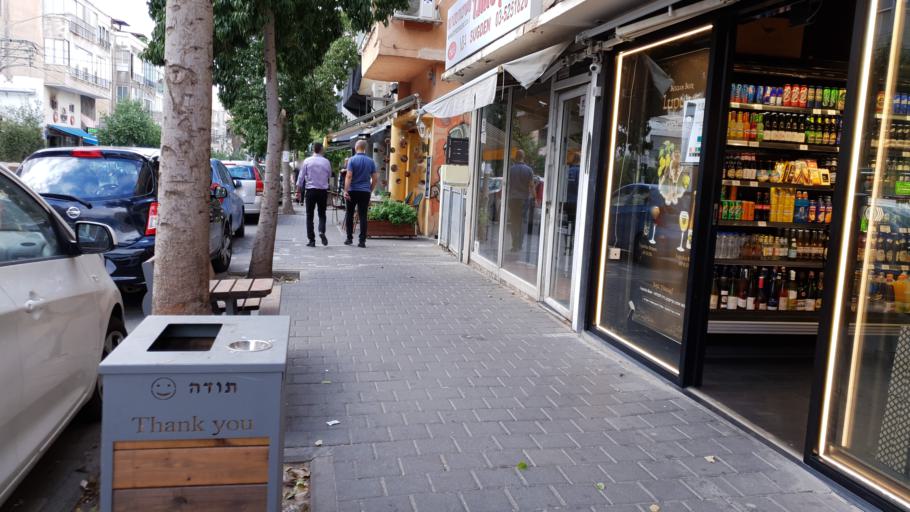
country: IL
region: Tel Aviv
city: Tel Aviv
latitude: 32.0762
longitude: 34.7712
